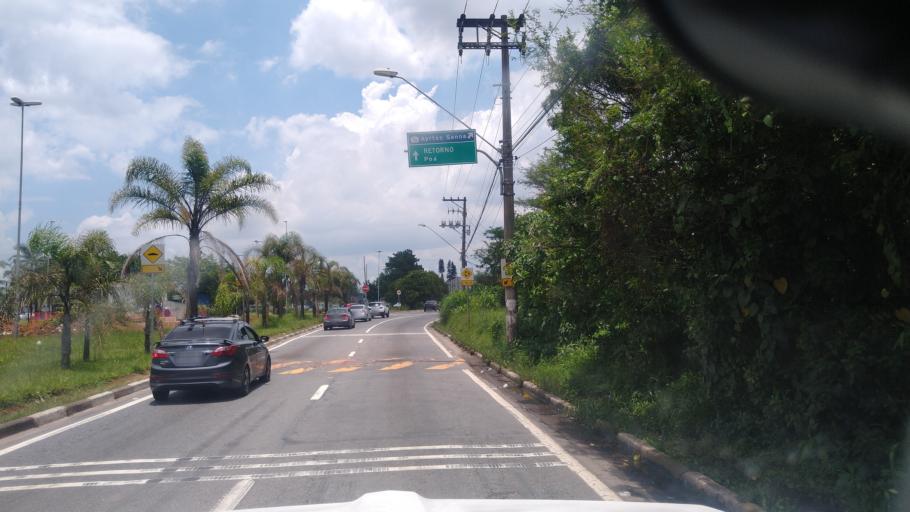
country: BR
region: Sao Paulo
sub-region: Poa
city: Poa
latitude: -23.5186
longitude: -46.3307
